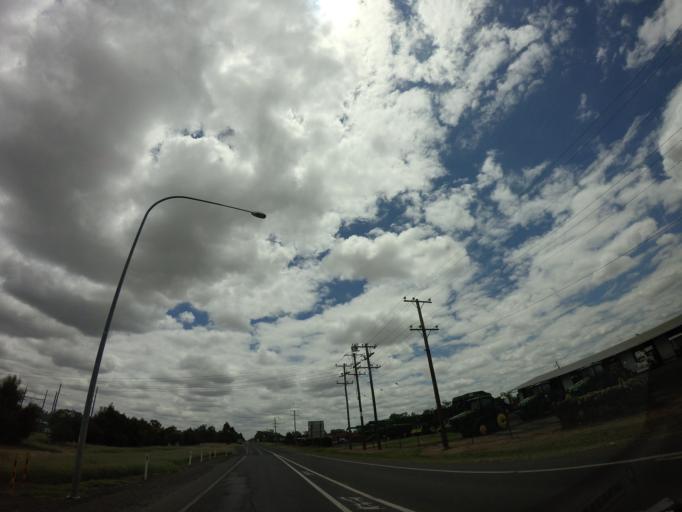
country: AU
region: Queensland
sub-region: Goondiwindi
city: Goondiwindi
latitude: -28.5253
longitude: 150.2870
